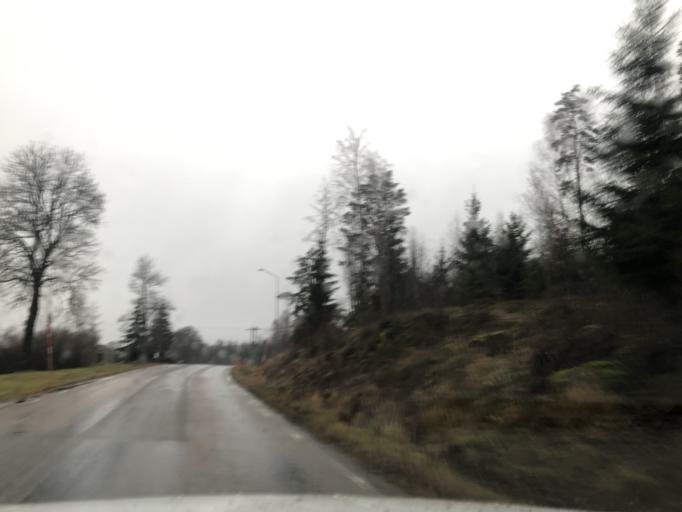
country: SE
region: Vaestra Goetaland
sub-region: Ulricehamns Kommun
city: Ulricehamn
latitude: 57.8348
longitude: 13.5316
